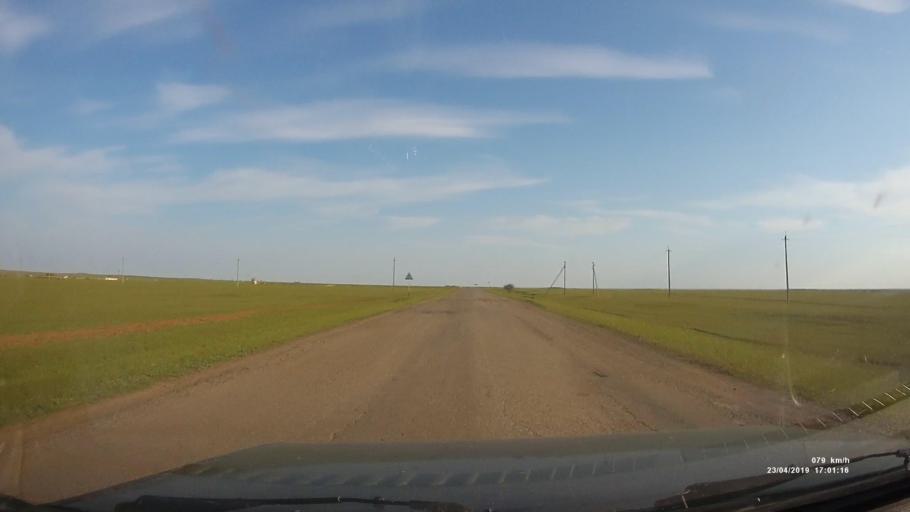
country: RU
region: Kalmykiya
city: Priyutnoye
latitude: 46.2981
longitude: 43.4074
